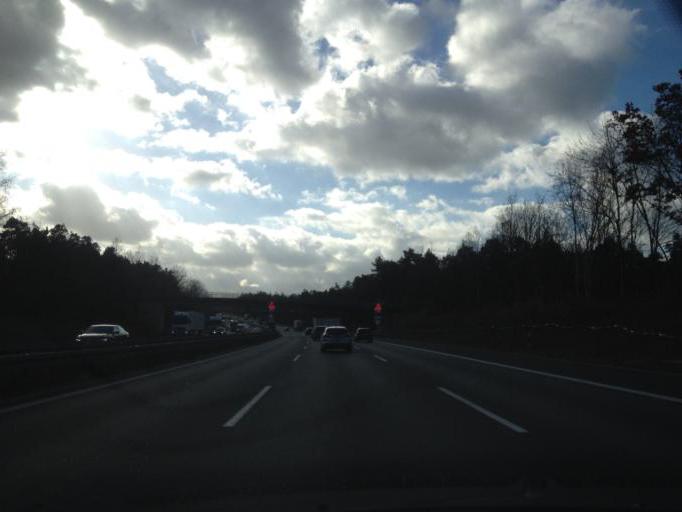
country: DE
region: Bavaria
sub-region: Regierungsbezirk Mittelfranken
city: Feucht
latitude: 49.4152
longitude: 11.1987
